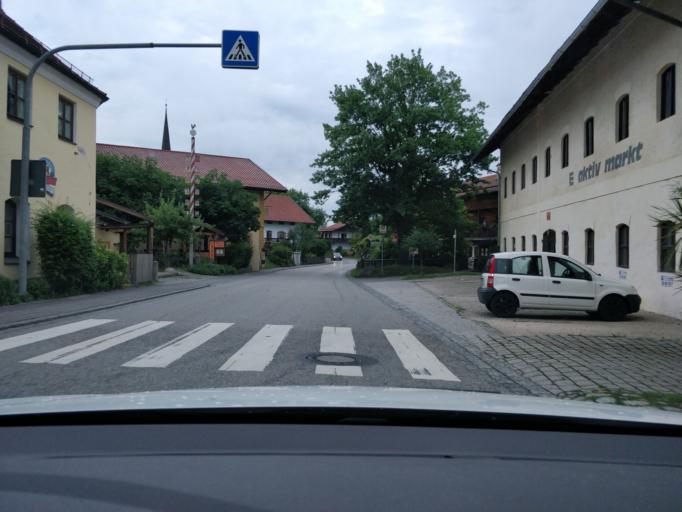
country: DE
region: Bavaria
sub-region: Upper Bavaria
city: Amerang
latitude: 47.9899
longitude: 12.3084
